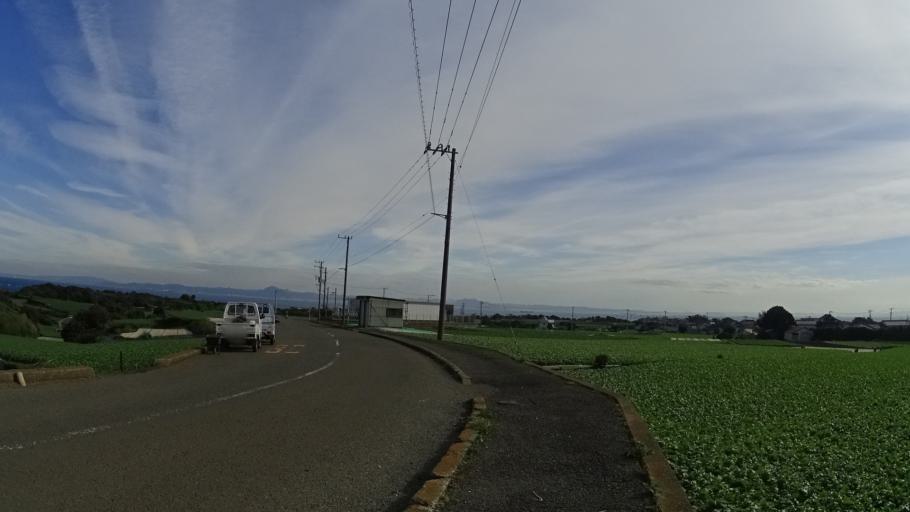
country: JP
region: Kanagawa
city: Miura
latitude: 35.1528
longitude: 139.6690
